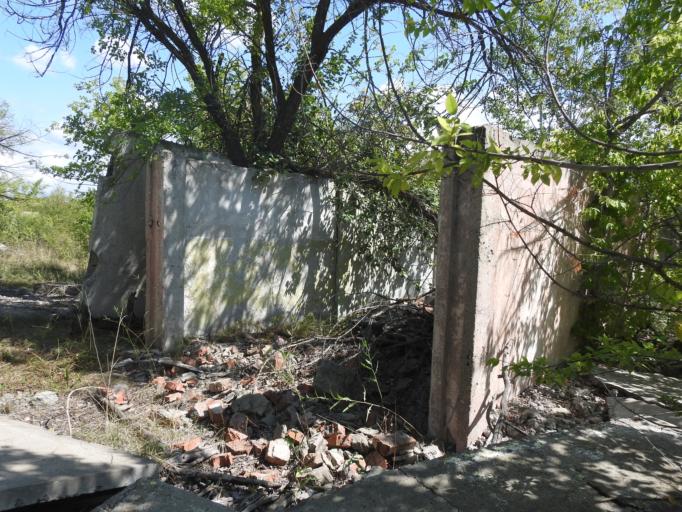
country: RU
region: Saratov
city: Engel's
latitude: 51.4353
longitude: 46.2258
